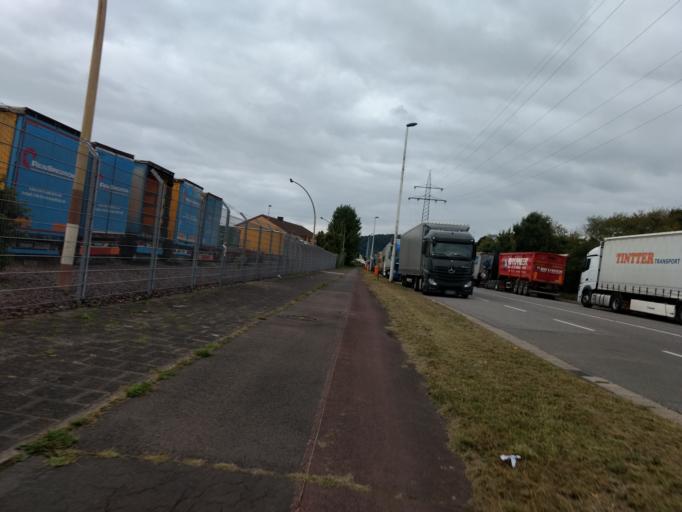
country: DE
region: Saarland
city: Dillingen
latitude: 49.3458
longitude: 6.7460
